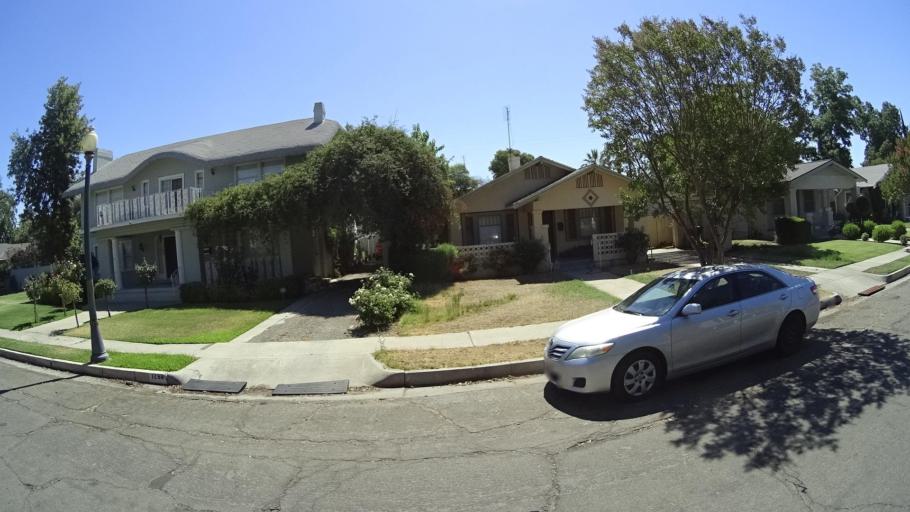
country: US
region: California
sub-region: Fresno County
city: Fresno
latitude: 36.7591
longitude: -119.8069
